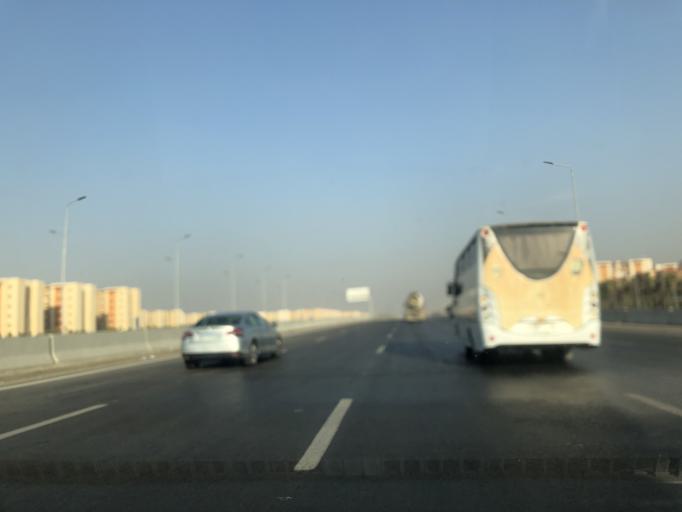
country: EG
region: Al Jizah
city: Madinat Sittah Uktubar
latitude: 29.9061
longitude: 30.9454
